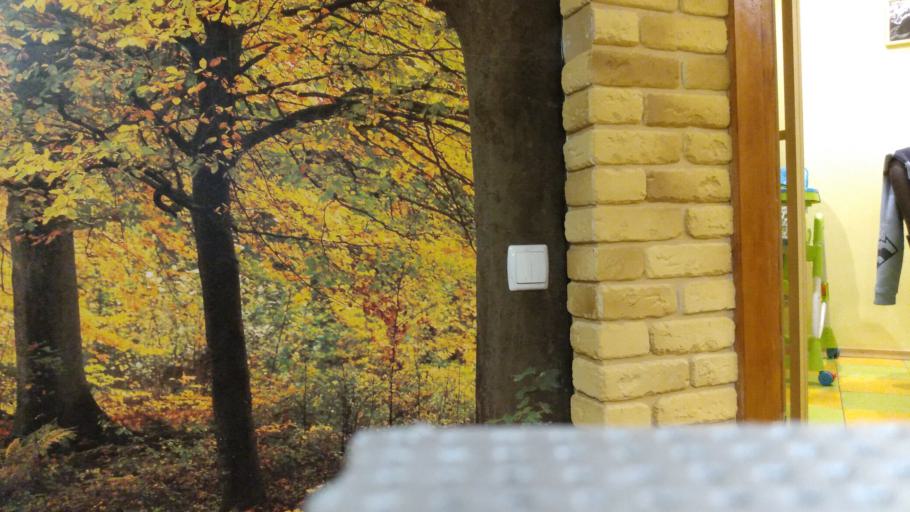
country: RU
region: Vologda
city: Babayevo
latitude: 59.3681
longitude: 35.9968
